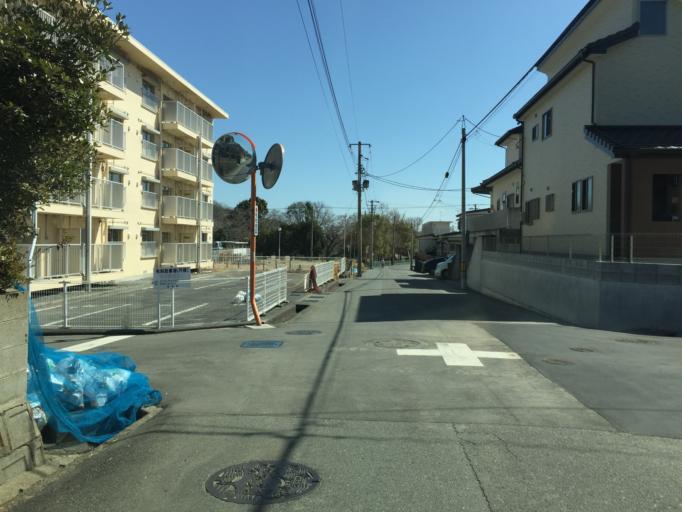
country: JP
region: Fukushima
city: Iwaki
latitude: 37.0486
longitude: 140.8552
